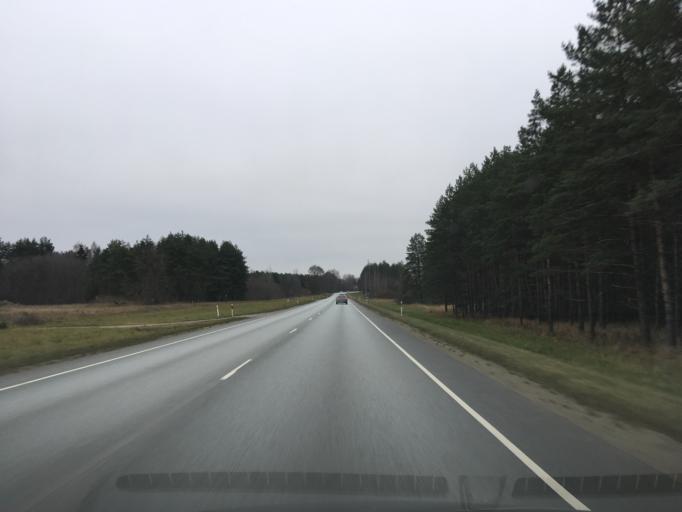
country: EE
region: Laeaene-Virumaa
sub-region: Viru-Nigula vald
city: Kunda
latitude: 59.4032
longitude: 26.6335
